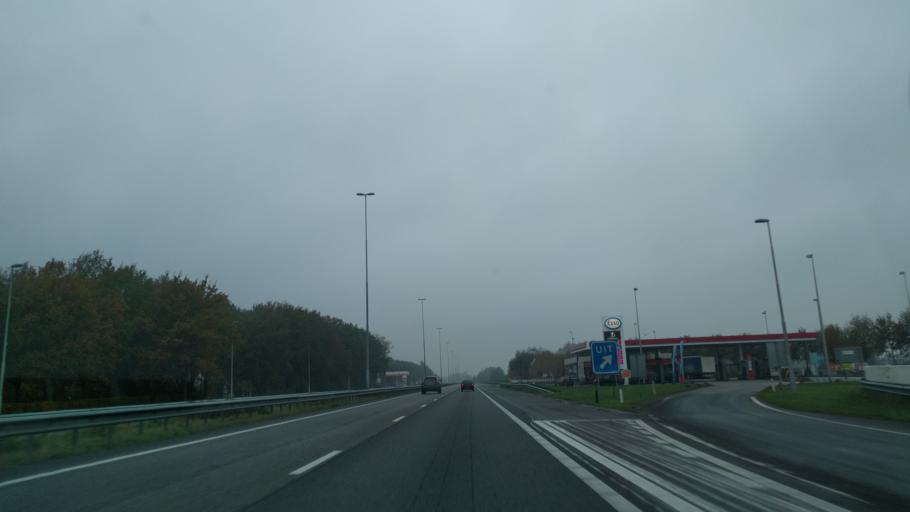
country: NL
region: North Brabant
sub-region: Gemeente Breda
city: Breda
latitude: 51.5740
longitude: 4.6889
